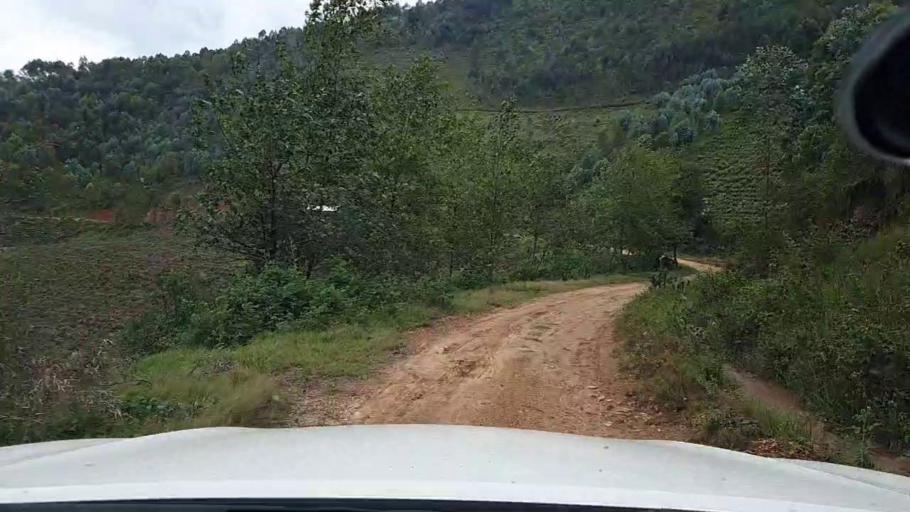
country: RW
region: Western Province
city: Kibuye
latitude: -2.1608
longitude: 29.4546
